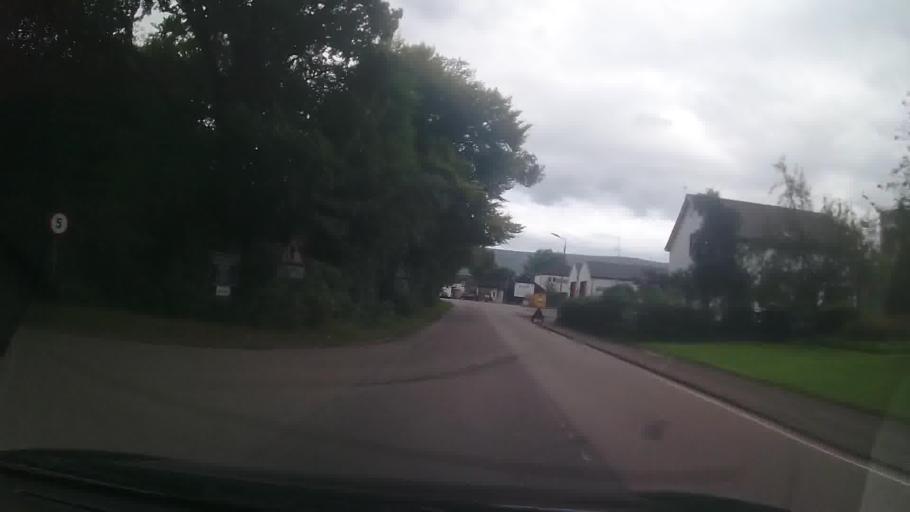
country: GB
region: Scotland
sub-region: Argyll and Bute
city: Garelochhead
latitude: 56.2320
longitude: -5.0760
